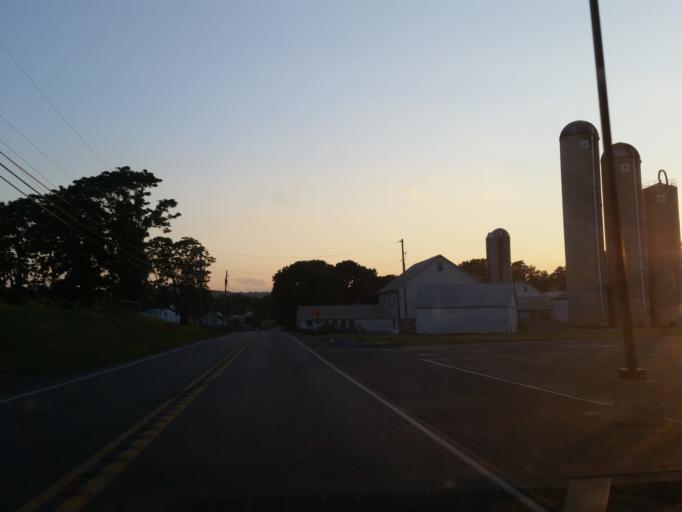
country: US
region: Pennsylvania
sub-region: Lancaster County
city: Brickerville
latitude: 40.2925
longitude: -76.3325
